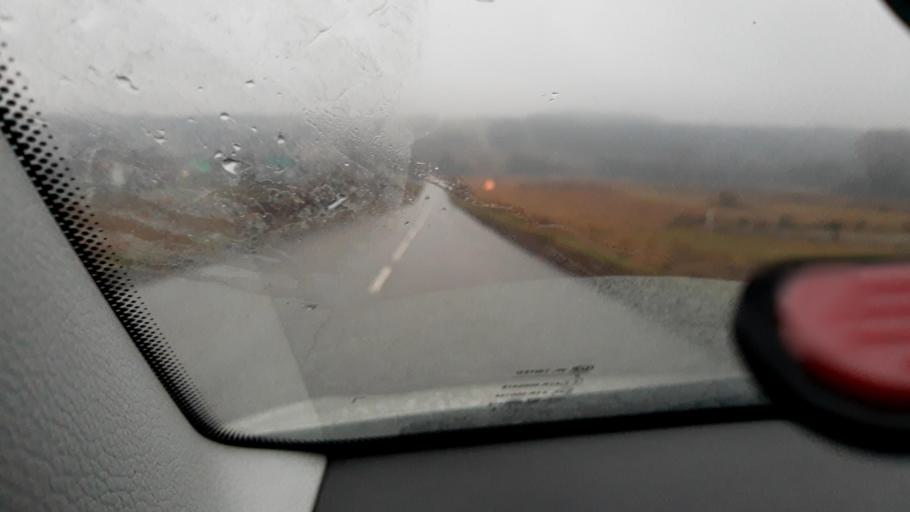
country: RU
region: Bashkortostan
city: Iglino
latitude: 54.9002
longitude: 56.1994
